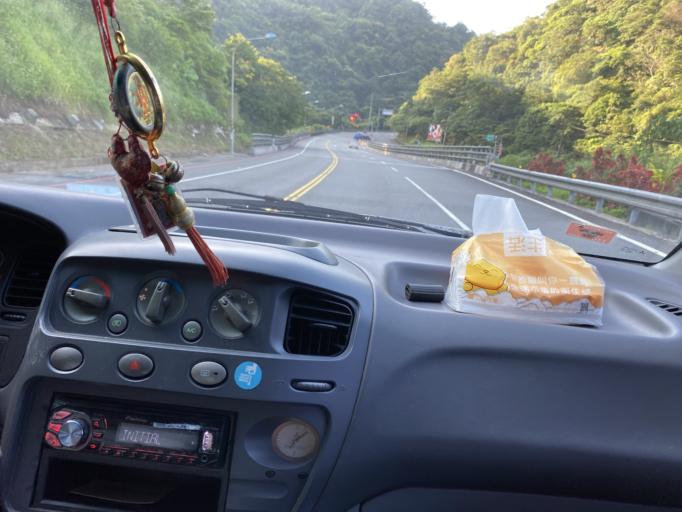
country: TW
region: Taiwan
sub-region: Keelung
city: Keelung
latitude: 25.0402
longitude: 121.7798
